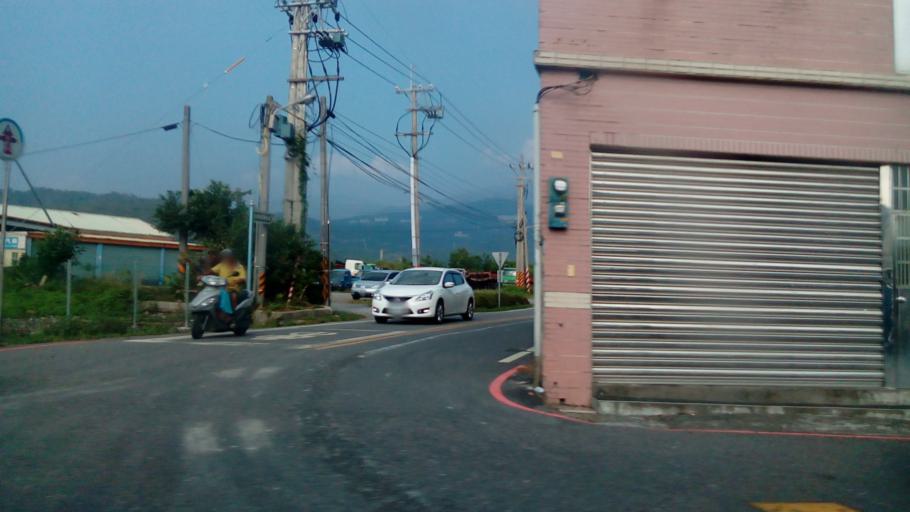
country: TW
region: Taiwan
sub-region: Yilan
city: Yilan
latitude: 24.8094
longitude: 121.7665
